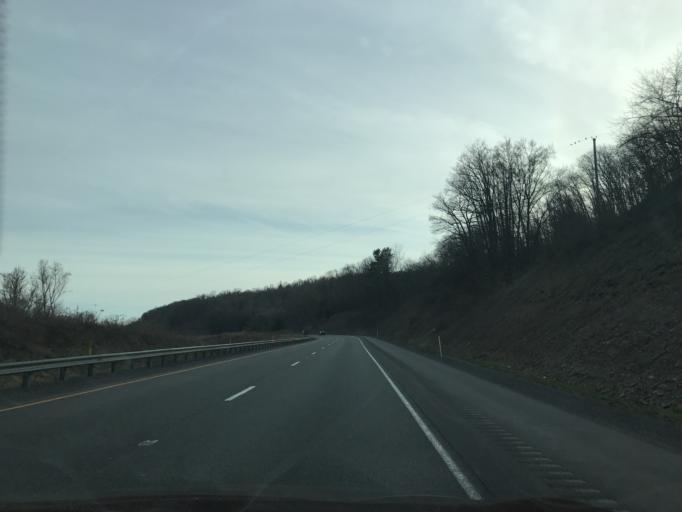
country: US
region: Pennsylvania
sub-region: Lycoming County
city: Muncy
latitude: 41.1616
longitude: -76.7948
